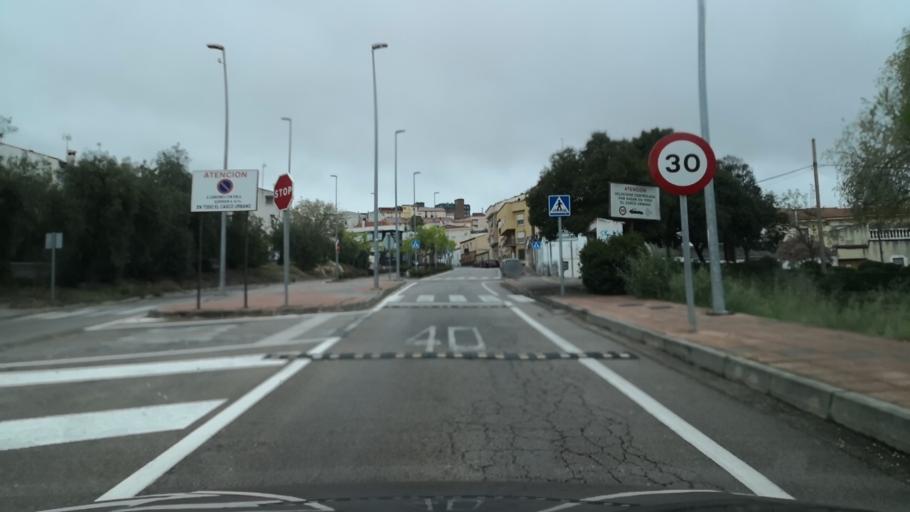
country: ES
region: Extremadura
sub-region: Provincia de Caceres
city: Caceres
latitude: 39.4816
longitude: -6.3797
